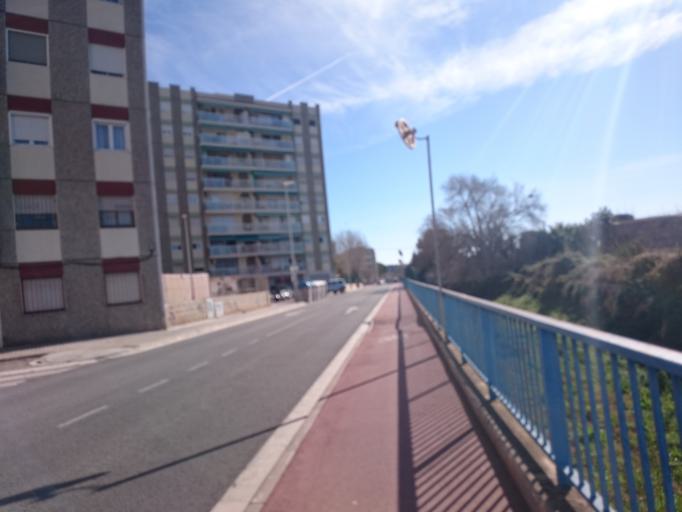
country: ES
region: Catalonia
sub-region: Provincia de Barcelona
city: Vilanova i la Geltru
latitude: 41.2184
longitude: 1.7179
